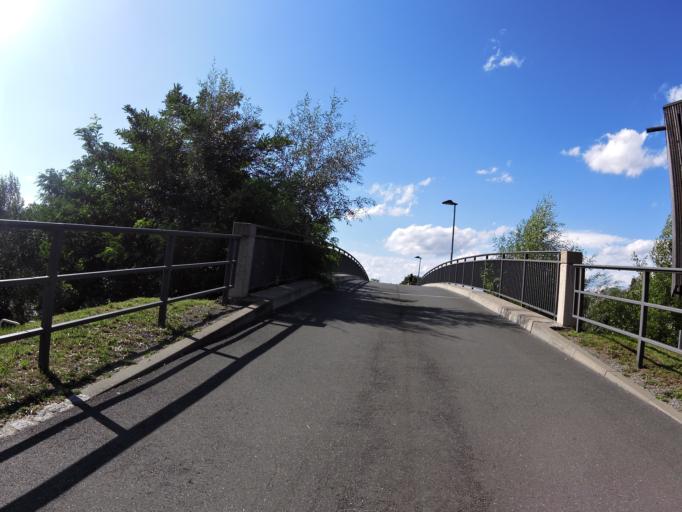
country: DE
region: Bavaria
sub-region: Regierungsbezirk Unterfranken
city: Kitzingen
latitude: 49.7332
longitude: 10.1698
